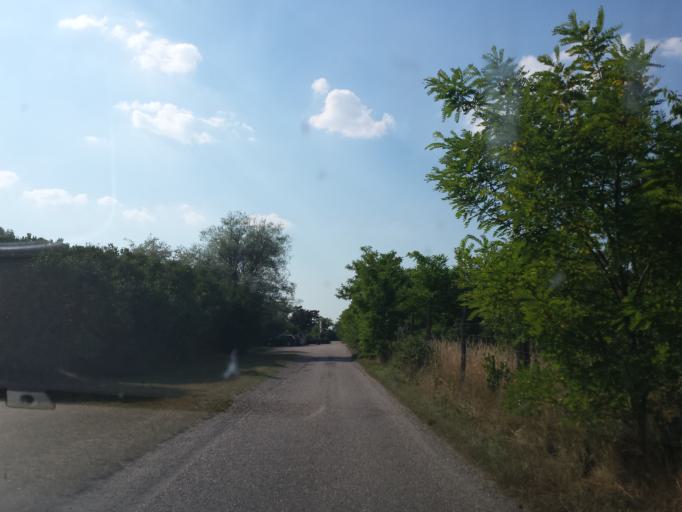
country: AT
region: Lower Austria
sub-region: Politischer Bezirk Ganserndorf
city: Lassee
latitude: 48.2764
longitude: 16.7912
